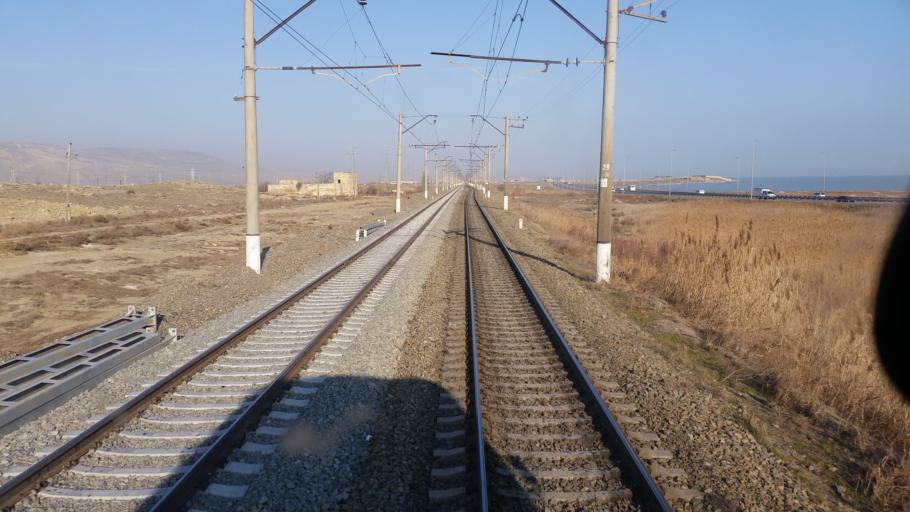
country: AZ
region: Baki
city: Qobustan
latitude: 40.1798
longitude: 49.4753
